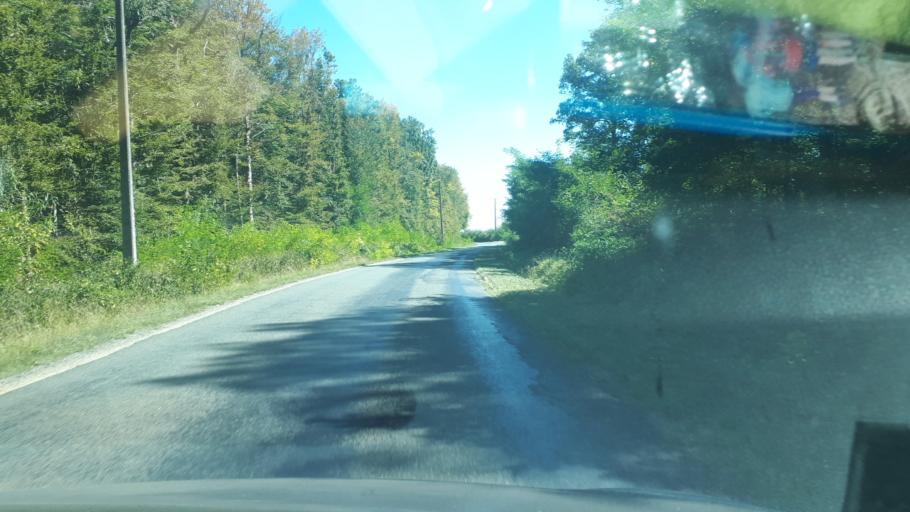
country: FR
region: Centre
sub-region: Departement du Cher
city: Rians
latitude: 47.1857
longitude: 2.6408
